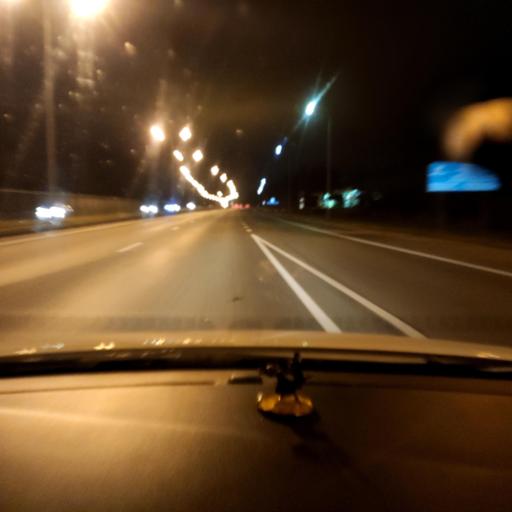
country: RU
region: Tatarstan
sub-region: Zelenodol'skiy Rayon
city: Vasil'yevo
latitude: 55.8710
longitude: 48.6709
